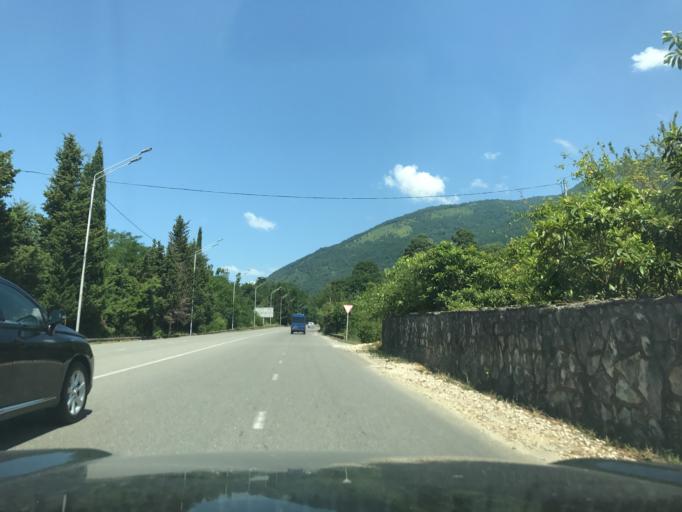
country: GE
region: Abkhazia
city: Gagra
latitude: 43.2607
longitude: 40.2942
